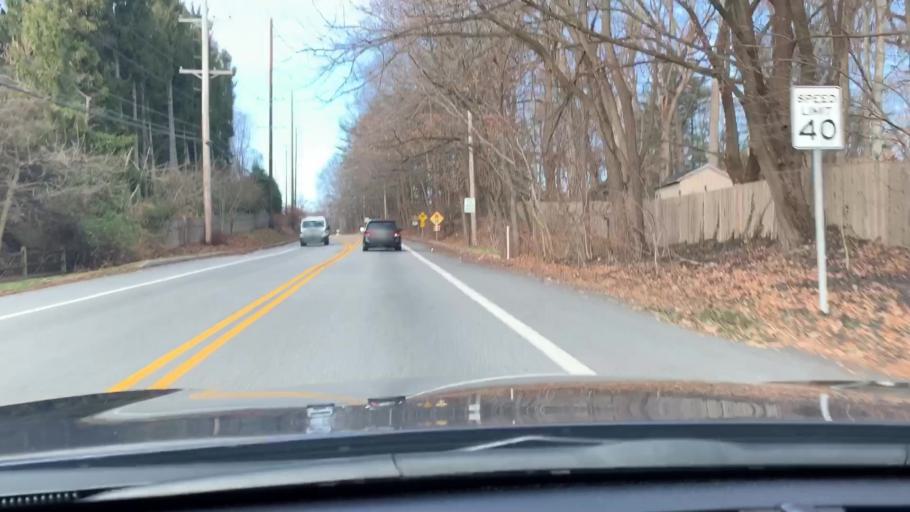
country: US
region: Pennsylvania
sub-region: Chester County
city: Paoli
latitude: 40.0338
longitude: -75.4692
